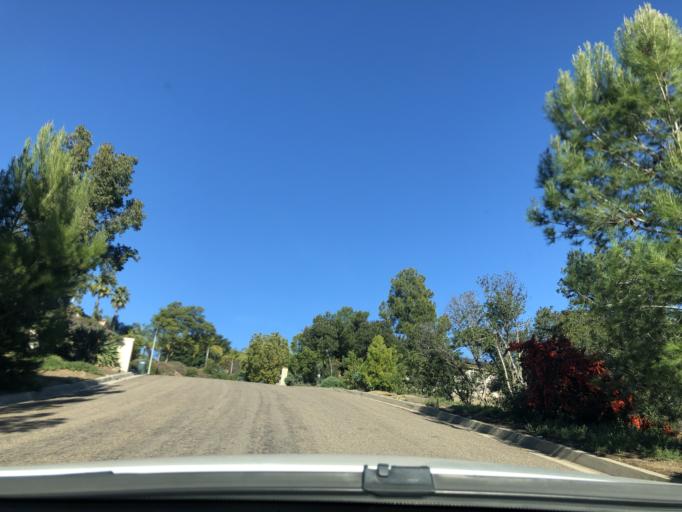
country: US
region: California
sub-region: San Diego County
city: Bostonia
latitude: 32.7805
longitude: -116.9385
